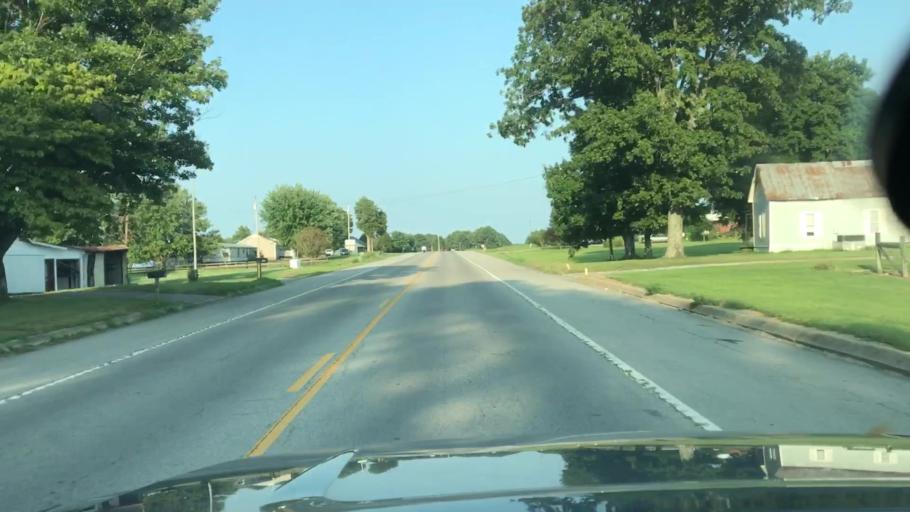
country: US
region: Tennessee
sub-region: Sumner County
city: Portland
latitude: 36.5782
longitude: -86.4378
